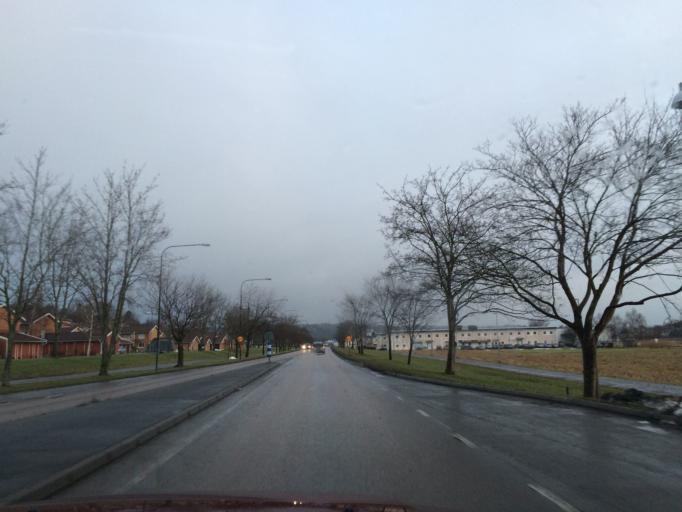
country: SE
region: Halland
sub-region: Kungsbacka Kommun
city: Kungsbacka
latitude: 57.4971
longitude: 12.0703
